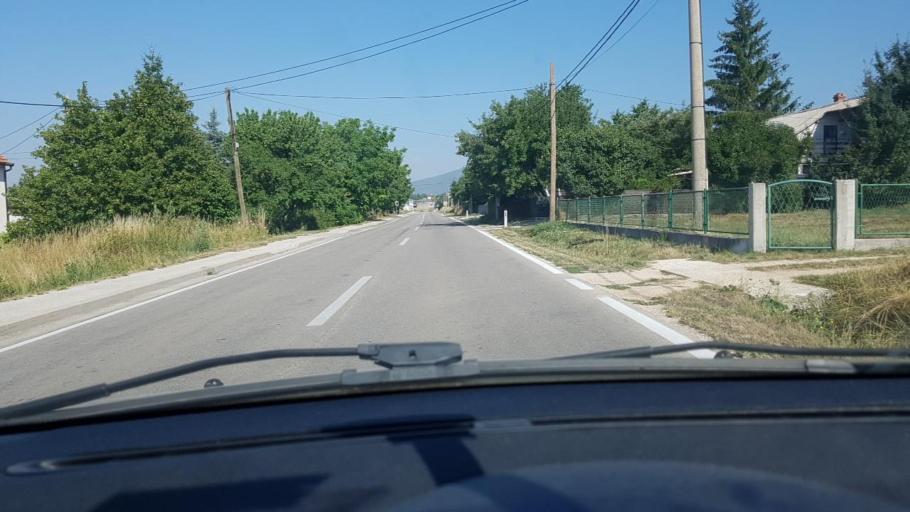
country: BA
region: Federation of Bosnia and Herzegovina
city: Livno
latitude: 43.8385
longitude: 16.9768
